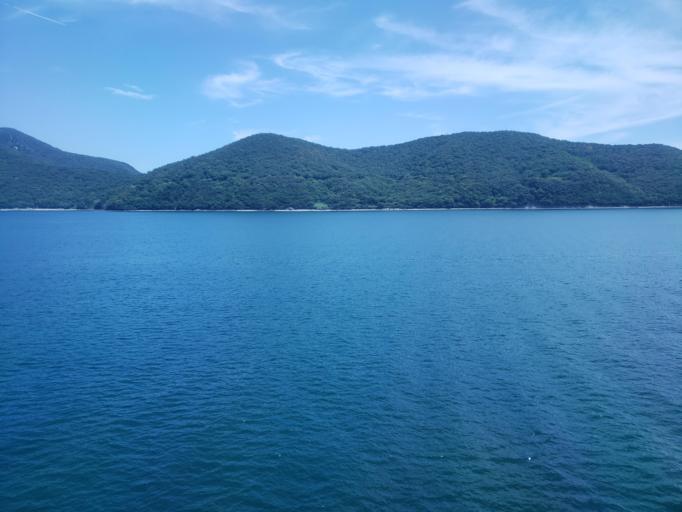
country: JP
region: Kagawa
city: Tonosho
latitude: 34.4342
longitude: 134.3227
